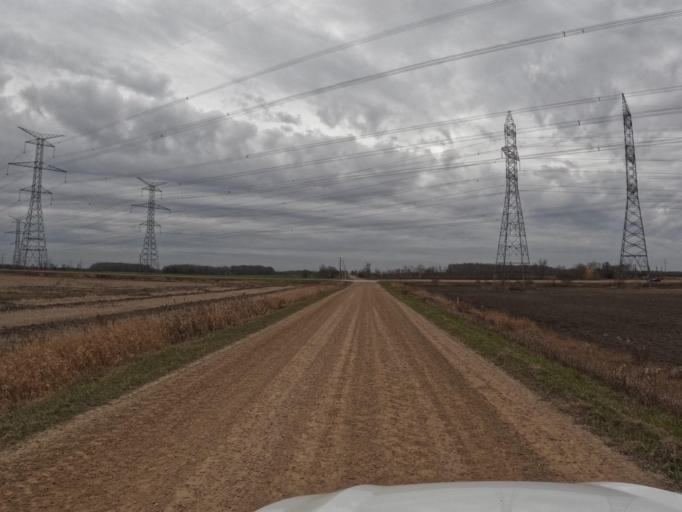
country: CA
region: Ontario
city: Shelburne
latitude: 43.9880
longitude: -80.3841
